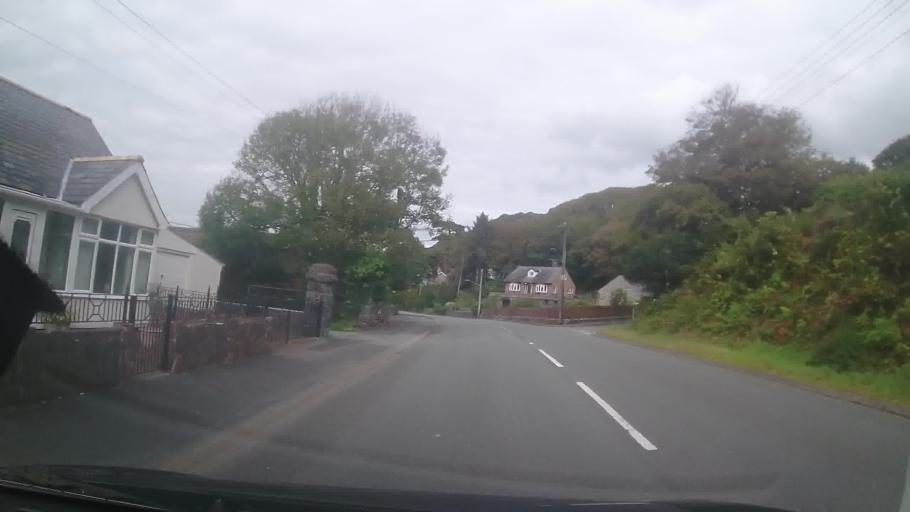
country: GB
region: Wales
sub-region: Gwynedd
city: Barmouth
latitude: 52.6908
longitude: -4.0478
